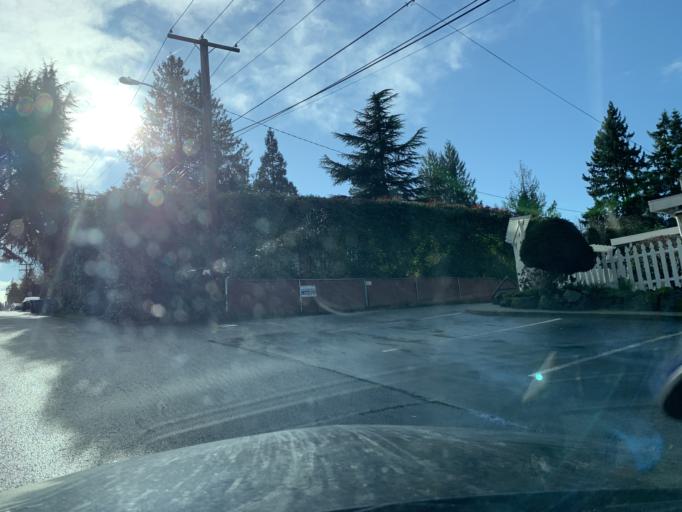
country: US
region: Washington
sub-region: King County
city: Medina
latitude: 47.5940
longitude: -122.2430
